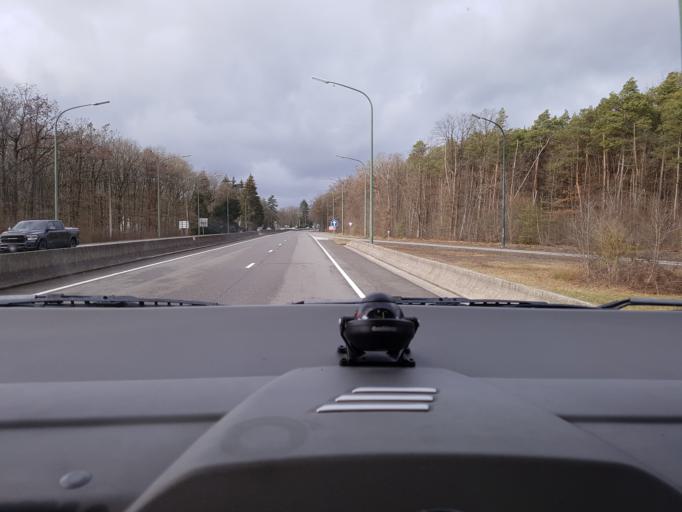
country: BE
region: Wallonia
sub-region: Province du Luxembourg
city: Marche-en-Famenne
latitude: 50.2339
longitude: 5.3081
